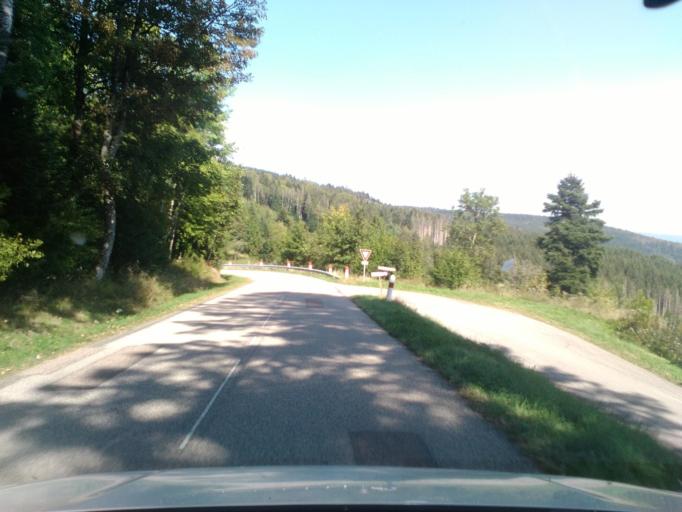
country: FR
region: Lorraine
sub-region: Departement des Vosges
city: Ban-de-Laveline
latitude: 48.3377
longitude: 7.0545
